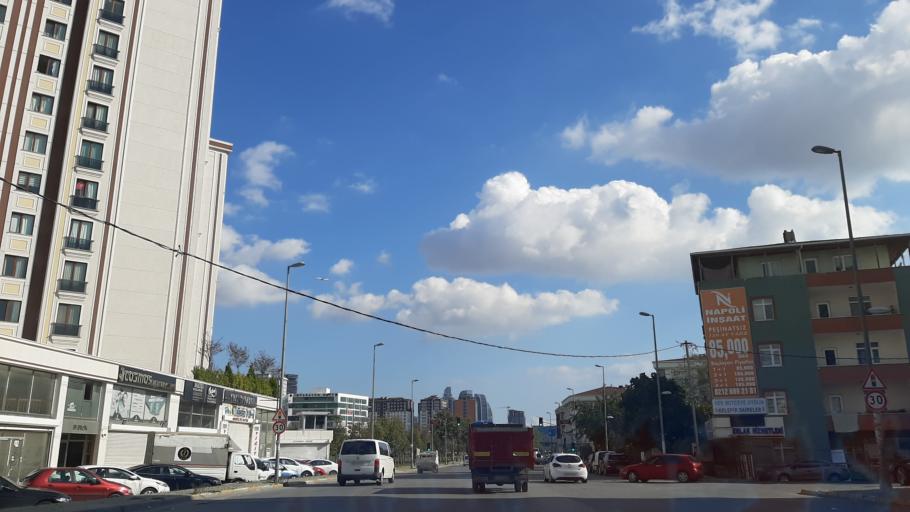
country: TR
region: Istanbul
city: Esenyurt
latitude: 41.0300
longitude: 28.6638
